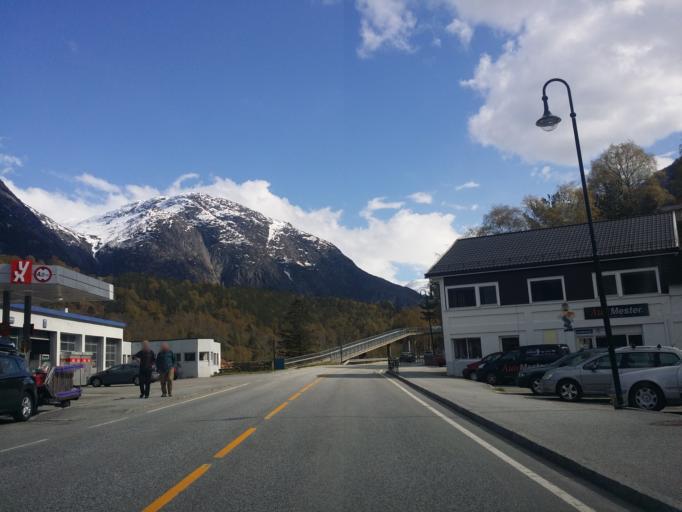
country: NO
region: Hordaland
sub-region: Eidfjord
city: Eidfjord
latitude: 60.4661
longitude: 7.0705
